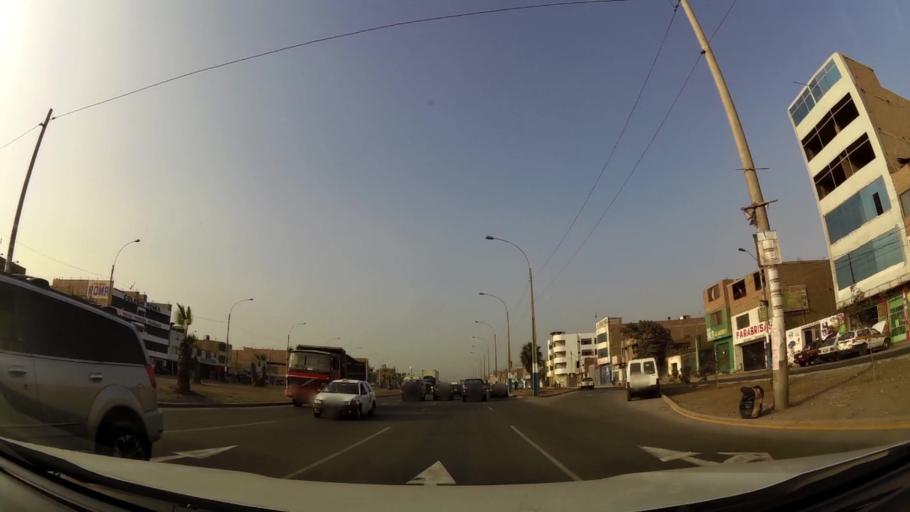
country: PE
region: Lima
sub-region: Lima
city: Independencia
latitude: -11.9801
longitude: -77.0954
